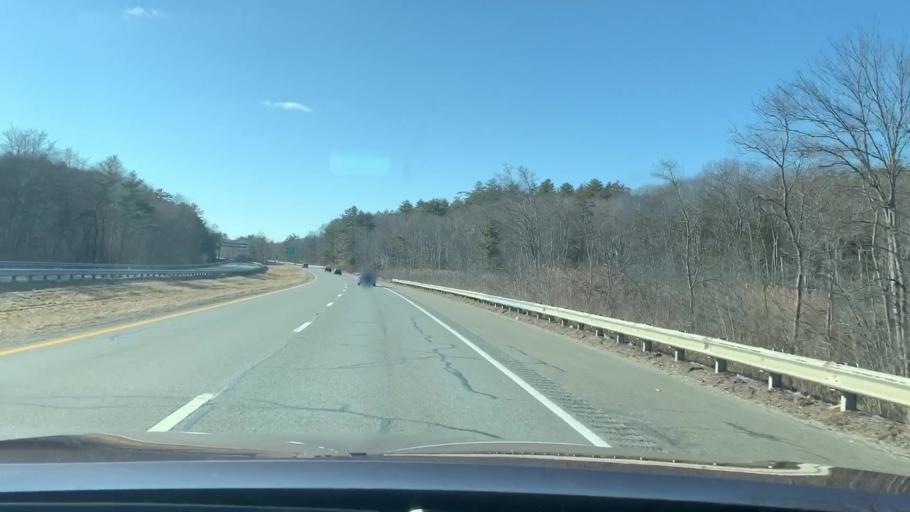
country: US
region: Massachusetts
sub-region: Essex County
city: Essex
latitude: 42.5913
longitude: -70.7738
